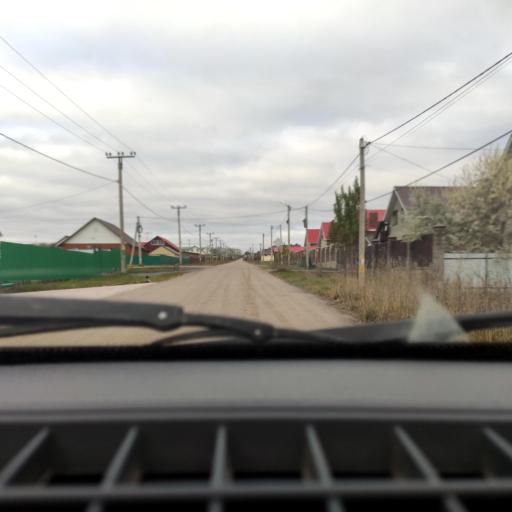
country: RU
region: Bashkortostan
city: Avdon
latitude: 54.6570
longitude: 55.7447
